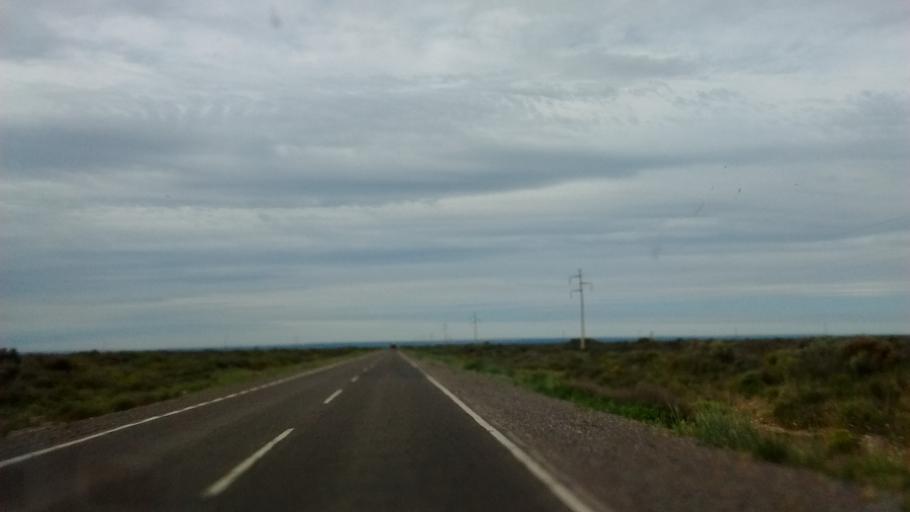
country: AR
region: Rio Negro
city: Catriel
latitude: -37.9433
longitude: -67.8865
